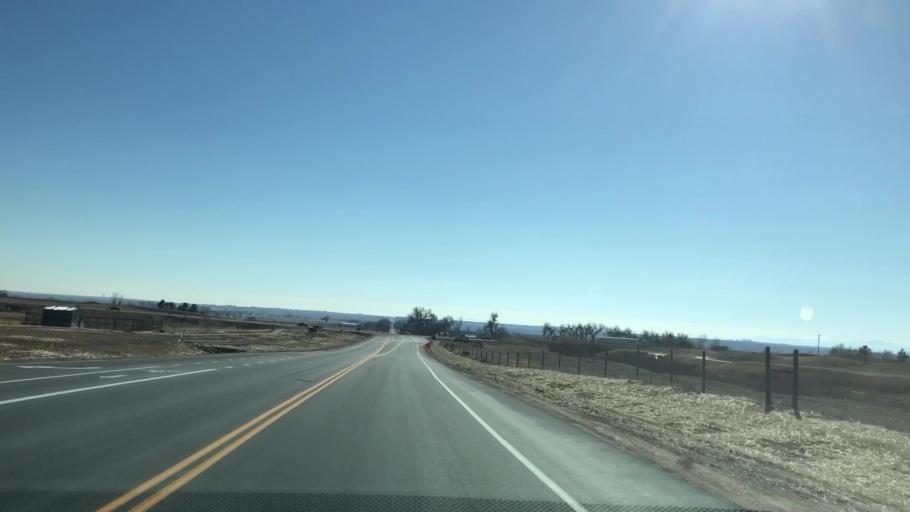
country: US
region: Colorado
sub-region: Weld County
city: Windsor
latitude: 40.5260
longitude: -104.9442
